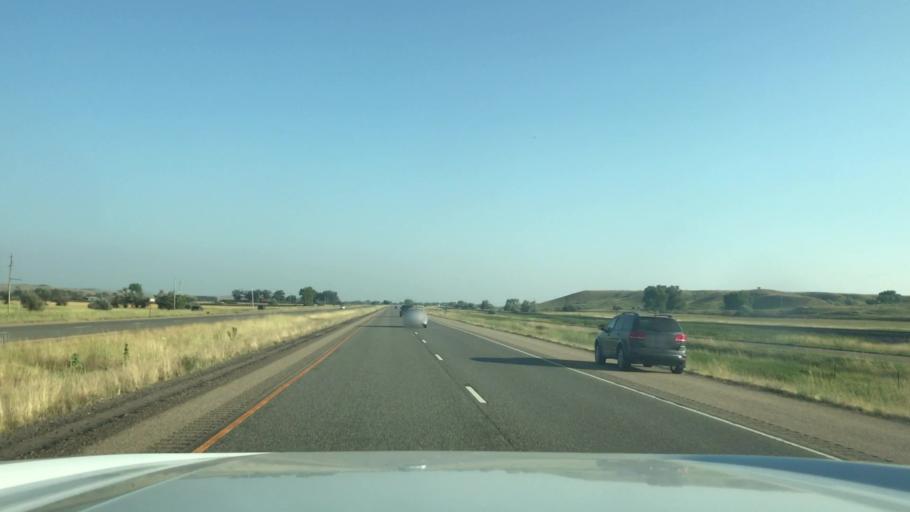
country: US
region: Montana
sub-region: Big Horn County
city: Crow Agency
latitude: 45.6353
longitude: -107.4697
